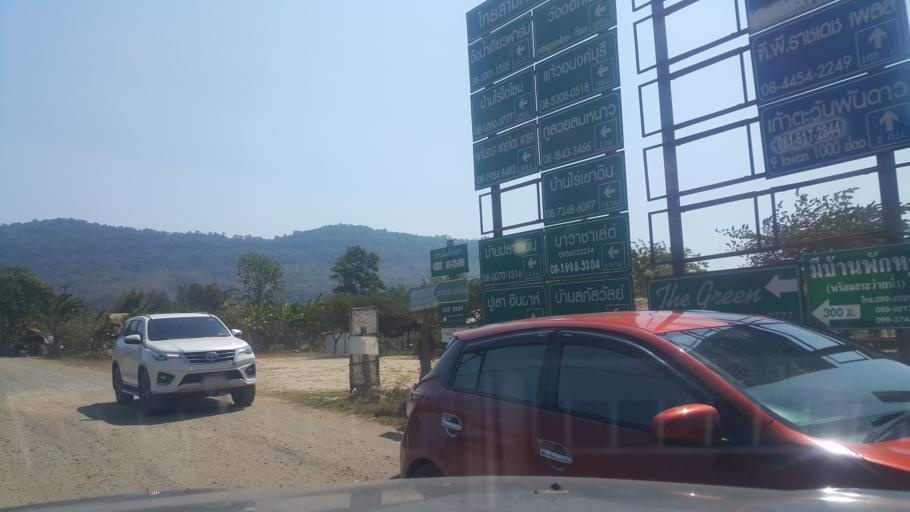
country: TH
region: Nakhon Ratchasima
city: Wang Nam Khiao
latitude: 14.3416
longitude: 101.9414
